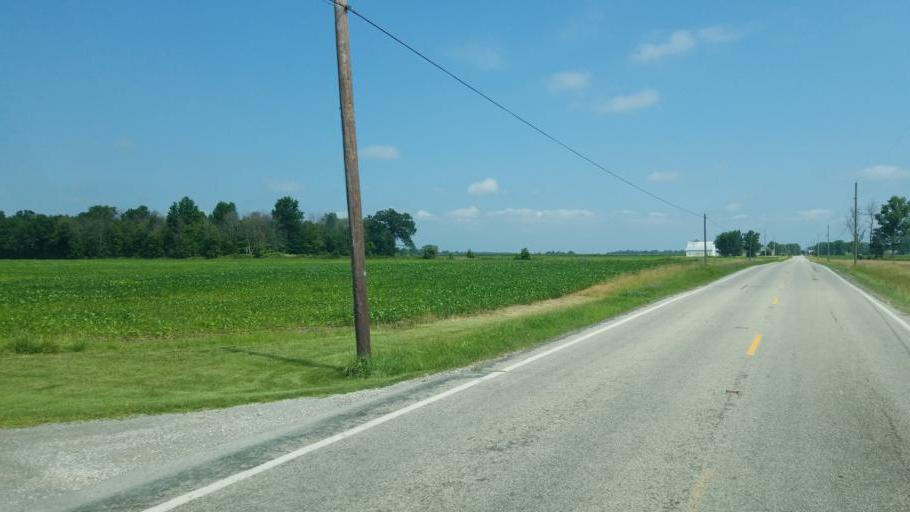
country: US
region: Ohio
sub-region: Crawford County
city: Galion
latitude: 40.7752
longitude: -82.8573
